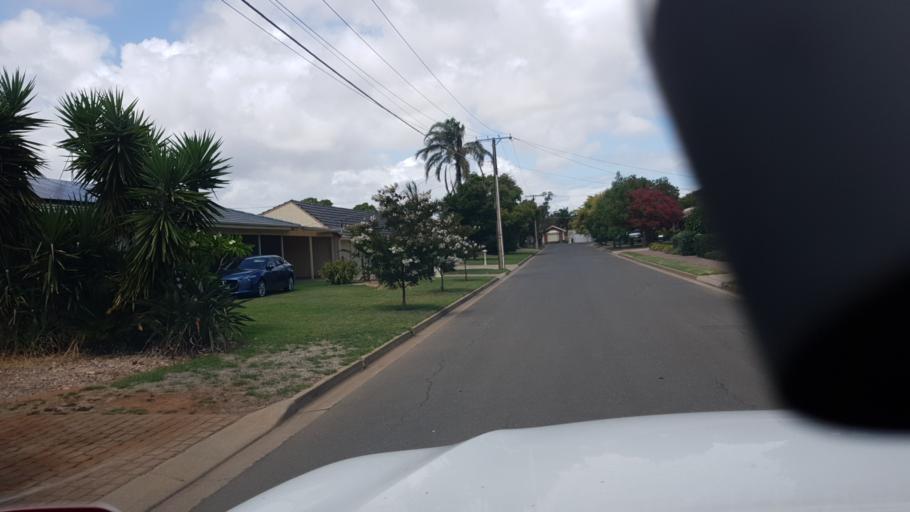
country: AU
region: South Australia
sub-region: Holdfast Bay
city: North Brighton
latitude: -35.0044
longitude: 138.5303
